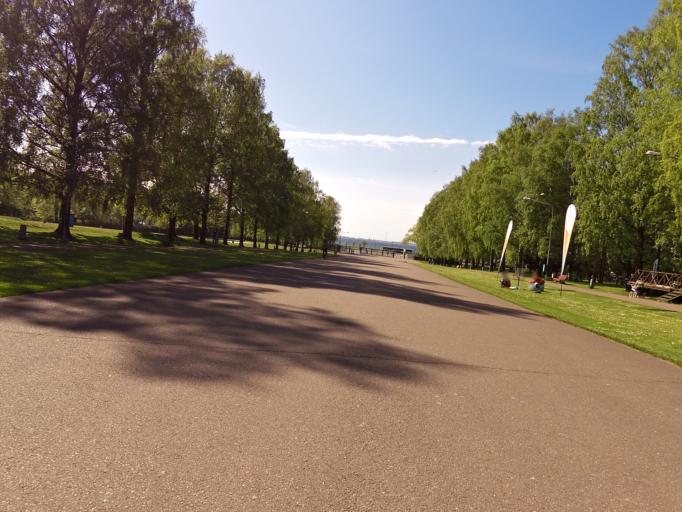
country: EE
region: Harju
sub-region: Tallinna linn
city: Tallinn
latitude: 59.4451
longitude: 24.8045
